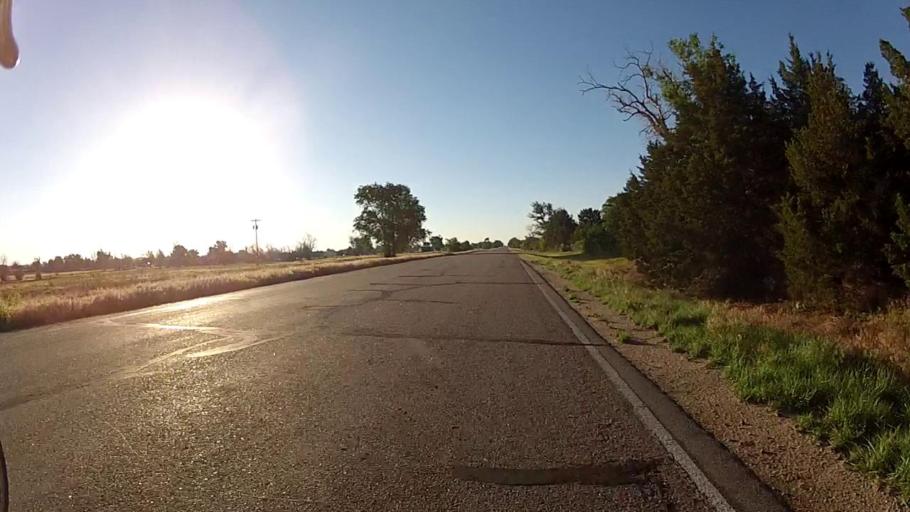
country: US
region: Kansas
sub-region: Ford County
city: Dodge City
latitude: 37.7163
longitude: -99.9367
